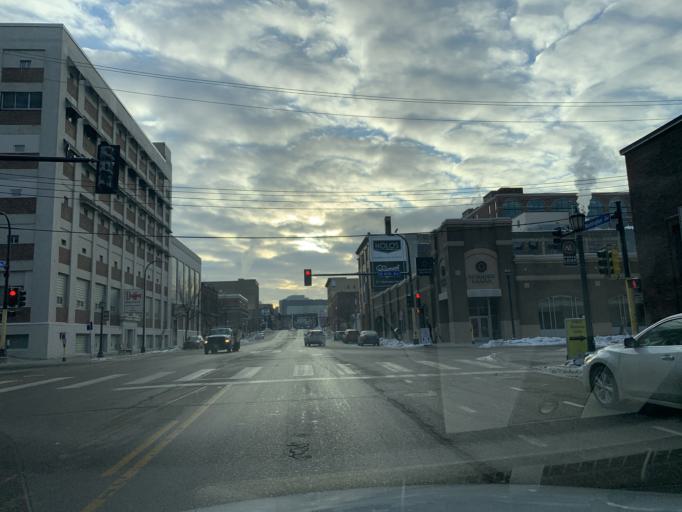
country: US
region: Minnesota
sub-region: Hennepin County
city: Minneapolis
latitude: 44.9871
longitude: -93.2762
